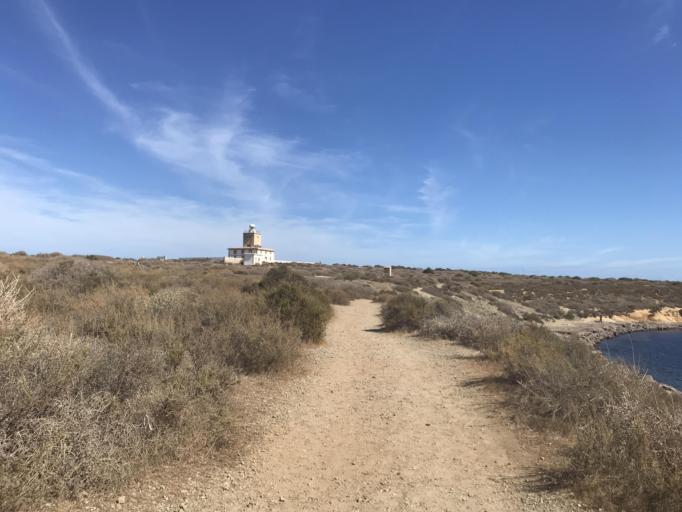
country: ES
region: Valencia
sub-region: Provincia de Alicante
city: Santa Pola
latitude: 38.1632
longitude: -0.4734
